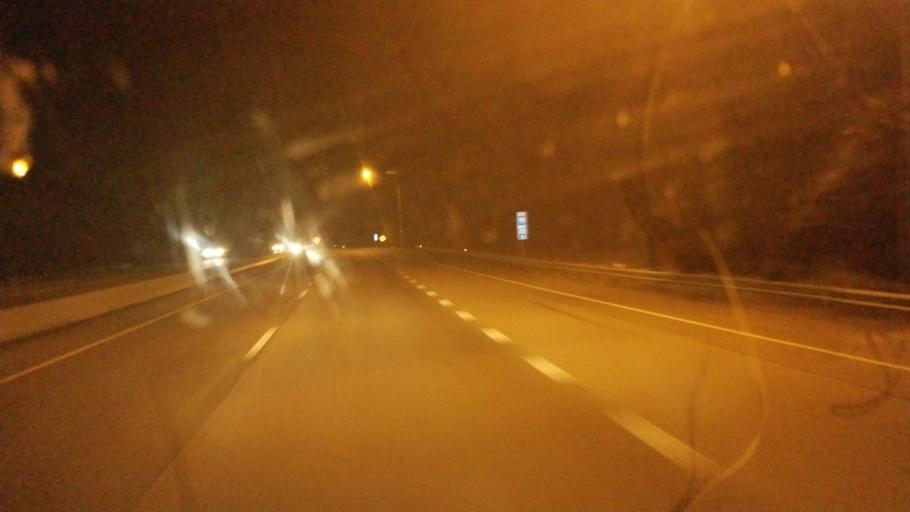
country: US
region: Ohio
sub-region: Belmont County
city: Saint Clairsville
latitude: 40.0747
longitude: -80.9224
